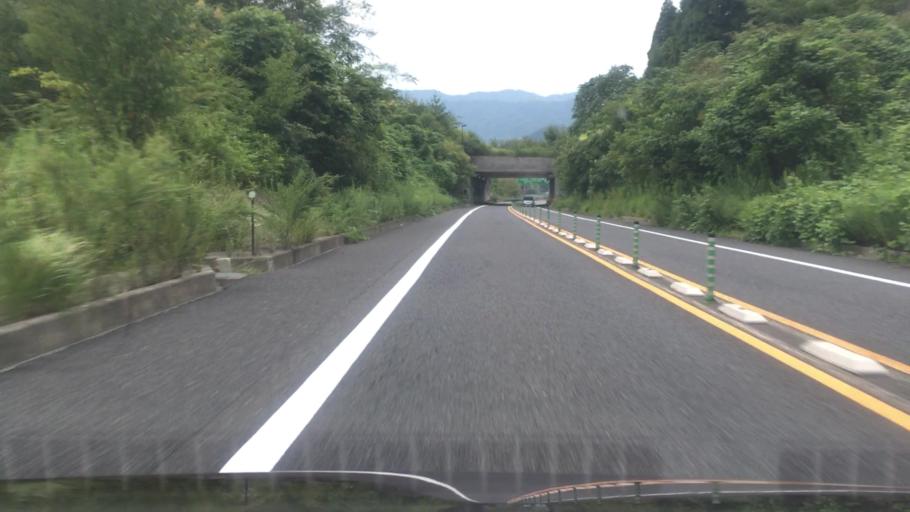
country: JP
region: Hyogo
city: Toyooka
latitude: 35.3099
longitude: 134.8629
